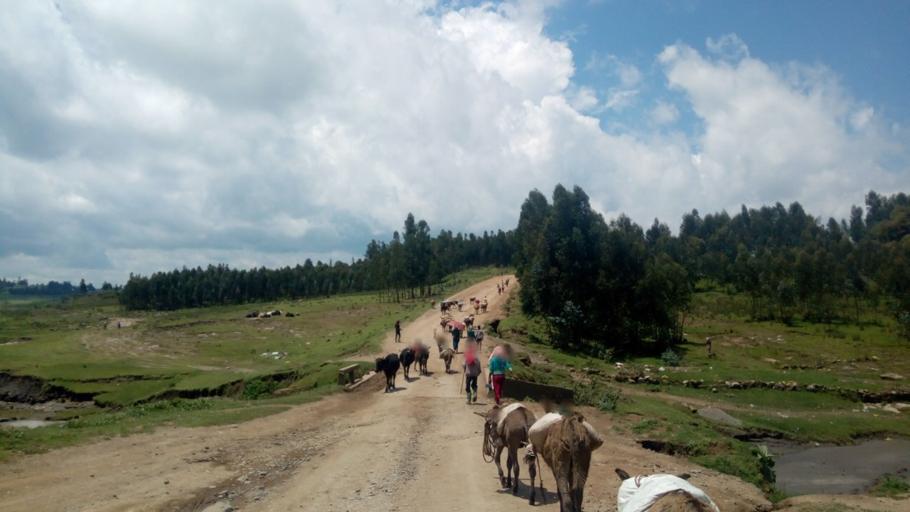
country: ET
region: Oromiya
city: Sendafa
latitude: 8.9782
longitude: 39.1237
